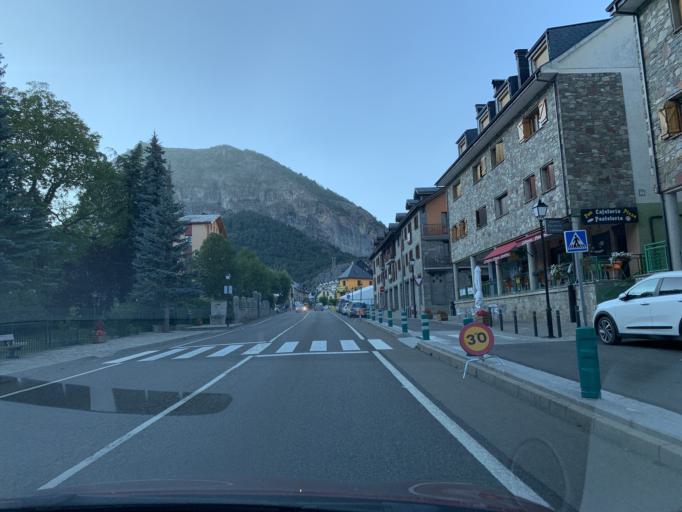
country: ES
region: Aragon
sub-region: Provincia de Huesca
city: Hoz de Jaca
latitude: 42.7320
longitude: -0.3110
